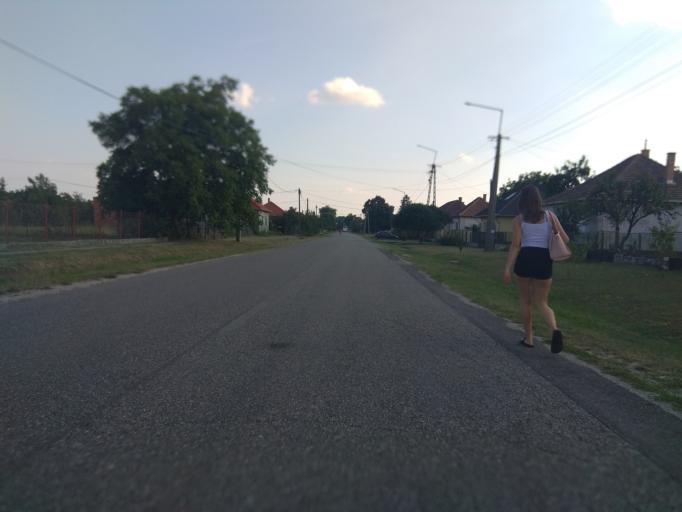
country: HU
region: Borsod-Abauj-Zemplen
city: Mezokeresztes
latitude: 47.8680
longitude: 20.6792
